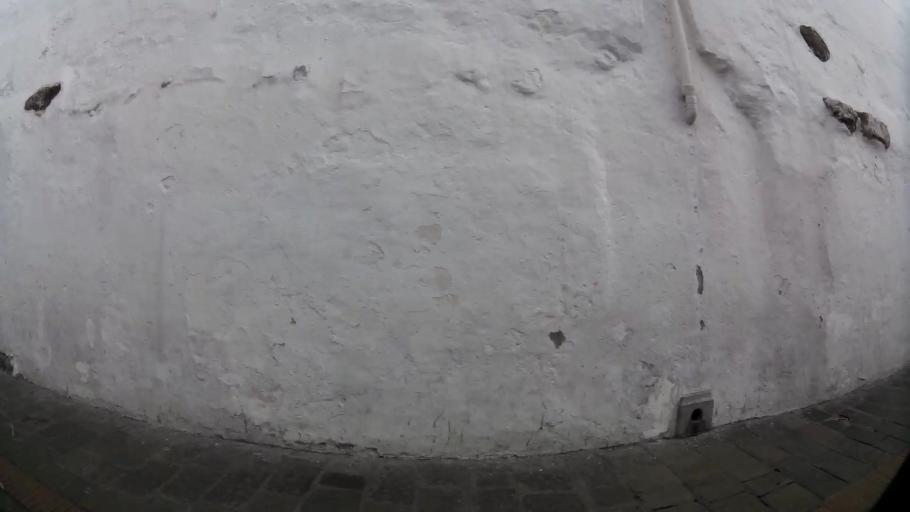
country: EC
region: Pichincha
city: Quito
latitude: -0.2230
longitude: -78.5153
